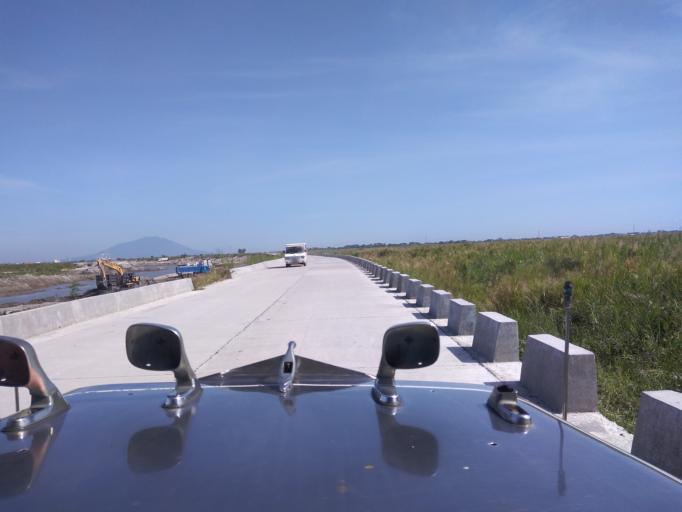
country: PH
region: Central Luzon
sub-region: Province of Pampanga
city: Minalin
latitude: 14.9813
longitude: 120.6843
